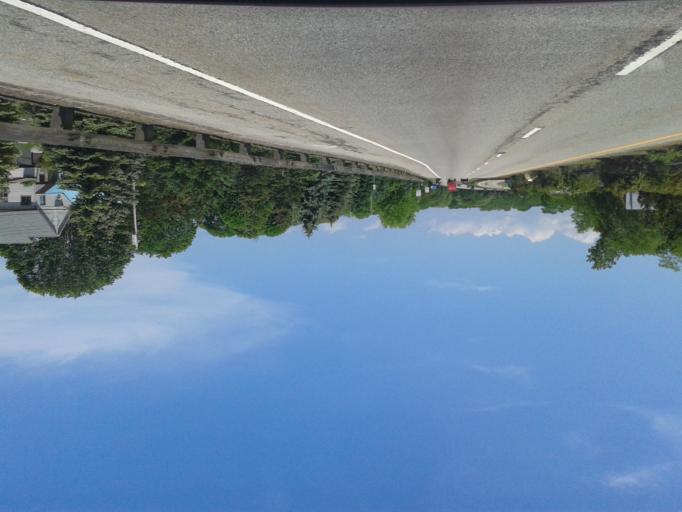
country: US
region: Rhode Island
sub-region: Newport County
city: Jamestown
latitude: 41.5151
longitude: -71.3667
